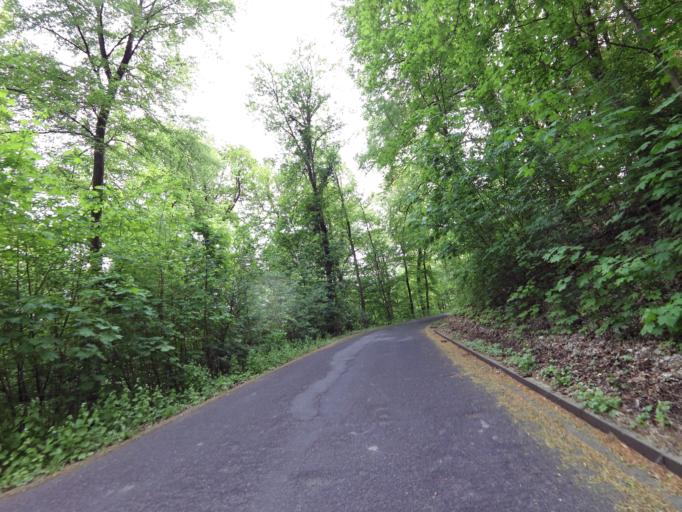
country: DE
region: North Rhine-Westphalia
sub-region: Regierungsbezirk Koln
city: Bonn
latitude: 50.6916
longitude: 7.1153
